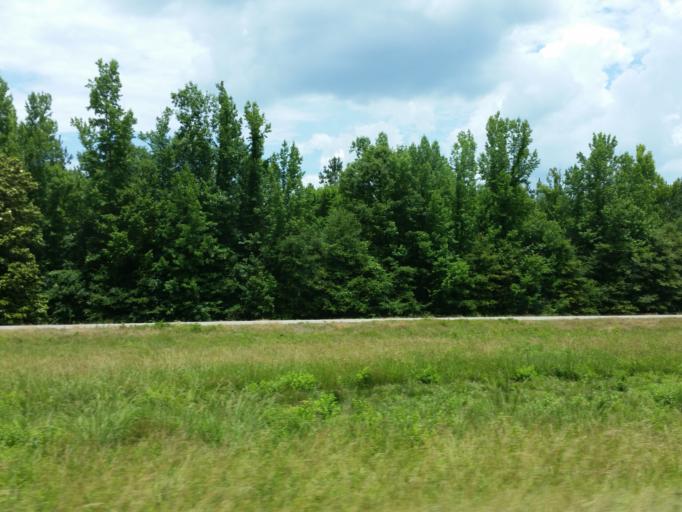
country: US
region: Mississippi
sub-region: Lauderdale County
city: Marion
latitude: 32.4126
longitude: -88.4914
